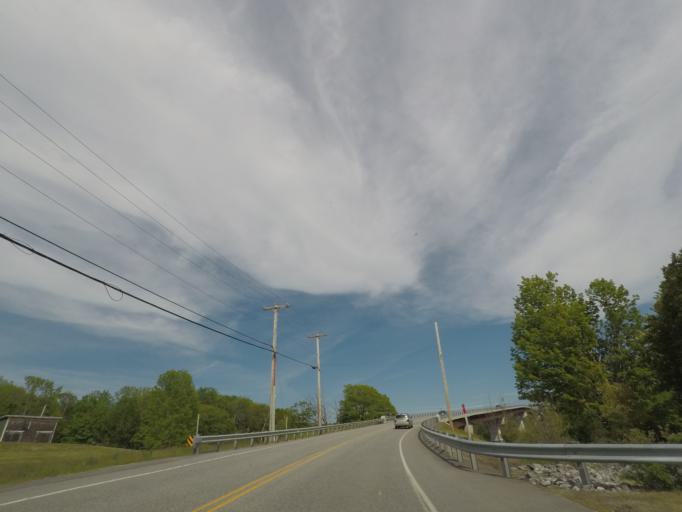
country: US
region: Maine
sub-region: Sagadahoc County
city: Richmond
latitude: 44.0920
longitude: -69.7857
